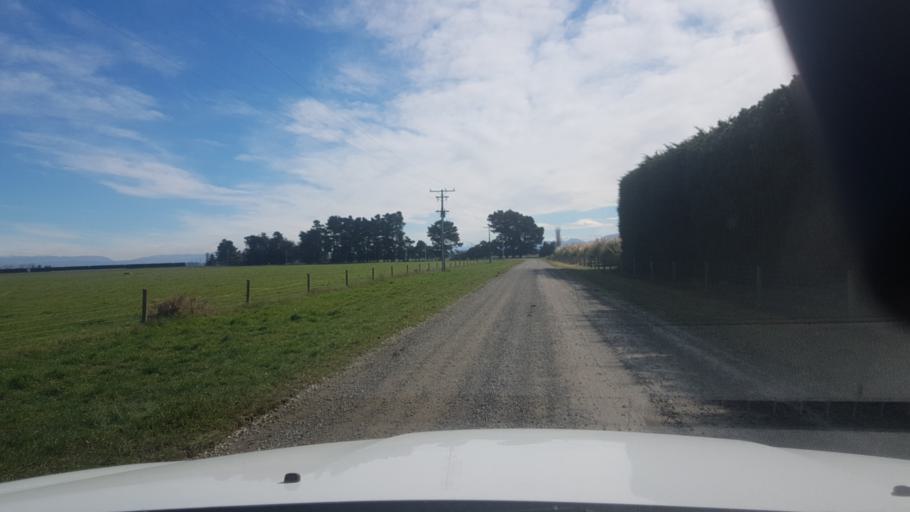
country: NZ
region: Canterbury
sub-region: Timaru District
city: Timaru
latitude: -44.2473
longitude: 171.3808
